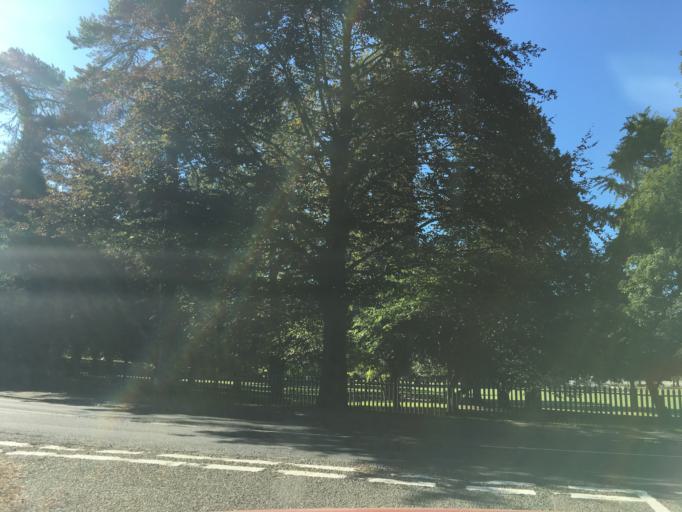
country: GB
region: England
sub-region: Wiltshire
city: Chippenham
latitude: 51.4669
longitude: -2.1203
